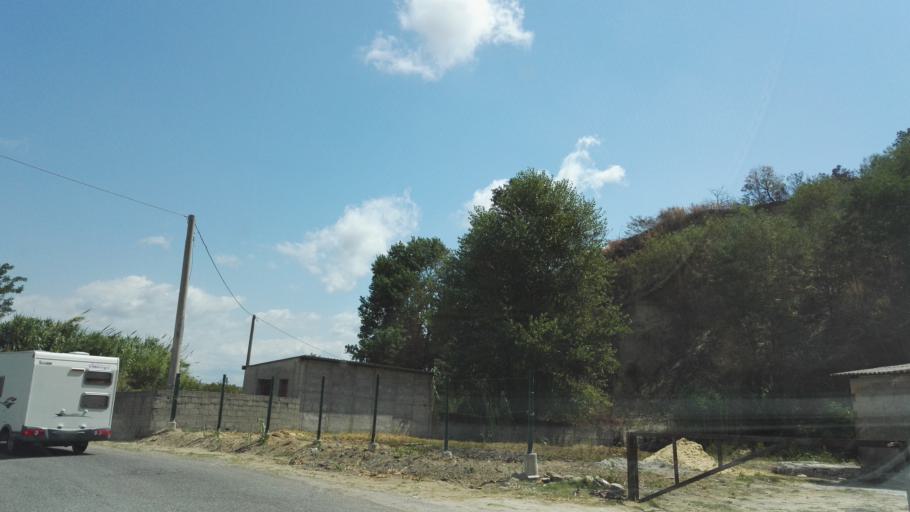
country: IT
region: Calabria
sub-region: Provincia di Reggio Calabria
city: Rosarno
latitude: 38.4963
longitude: 16.0086
